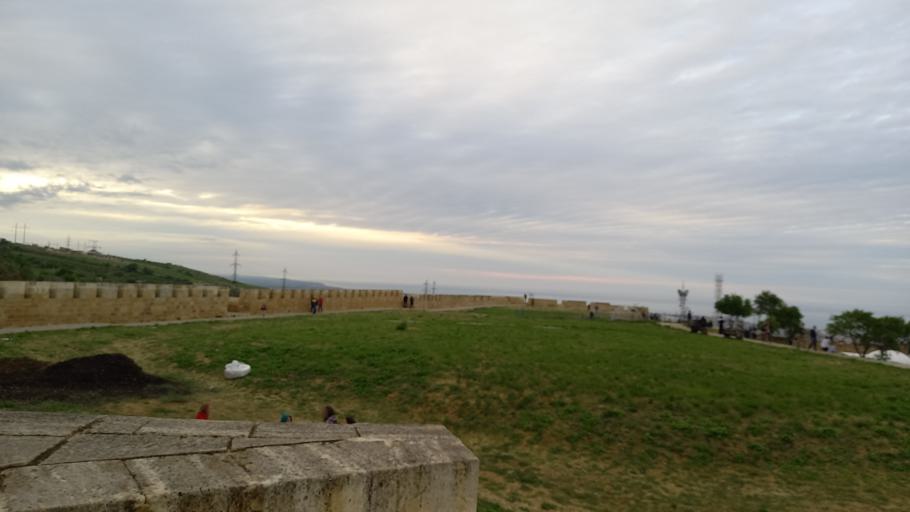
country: RU
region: Dagestan
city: Derbent
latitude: 42.0525
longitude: 48.2735
